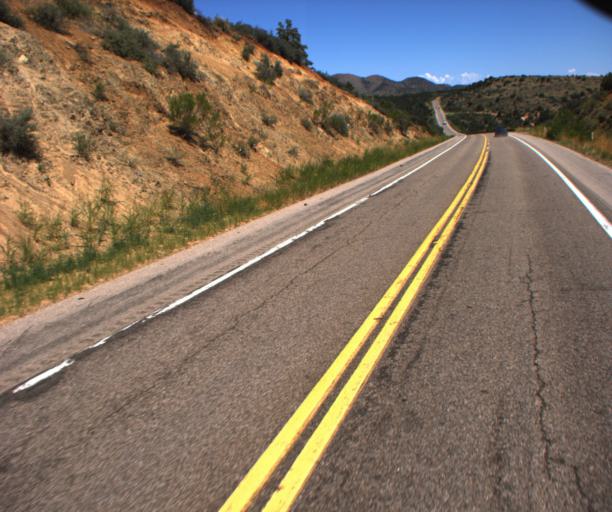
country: US
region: Arizona
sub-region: Gila County
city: Globe
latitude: 33.5334
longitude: -110.6928
